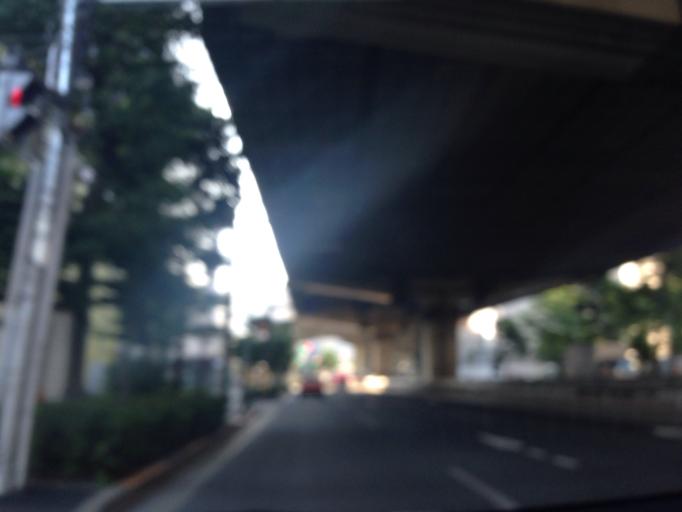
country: JP
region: Tokyo
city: Urayasu
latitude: 35.6582
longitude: 139.8085
